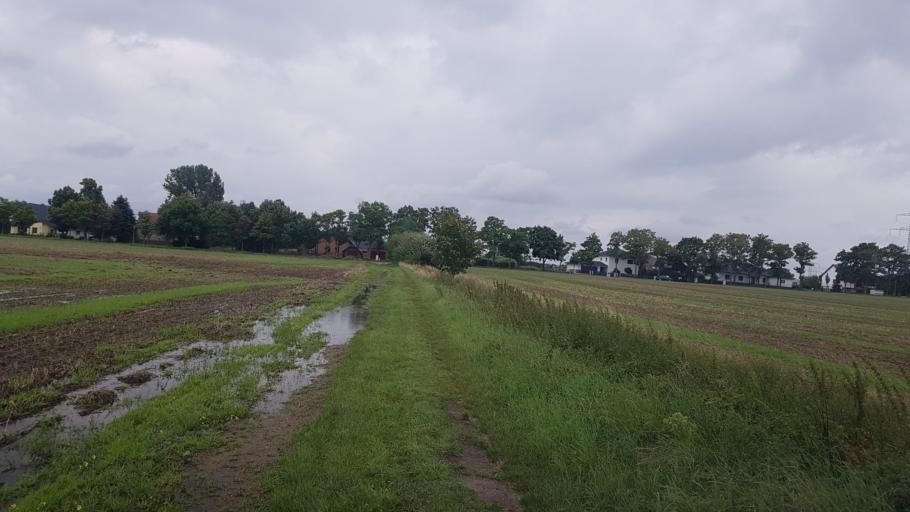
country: DE
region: Brandenburg
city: Doberlug-Kirchhain
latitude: 51.6386
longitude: 13.5428
